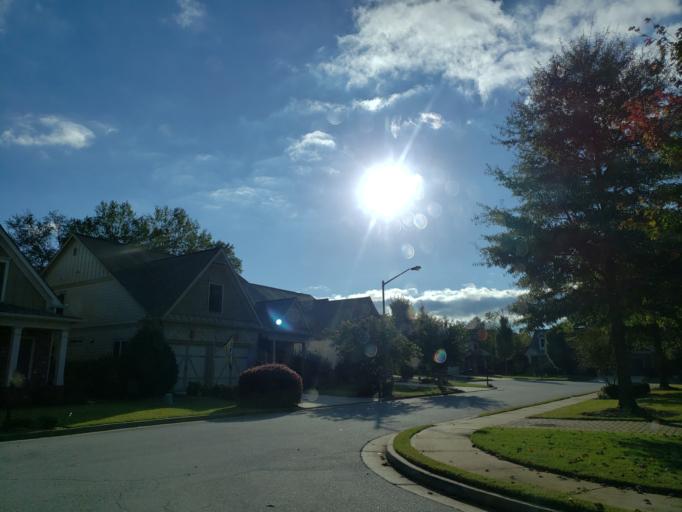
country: US
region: Georgia
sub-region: Cobb County
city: Marietta
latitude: 33.9901
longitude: -84.5049
